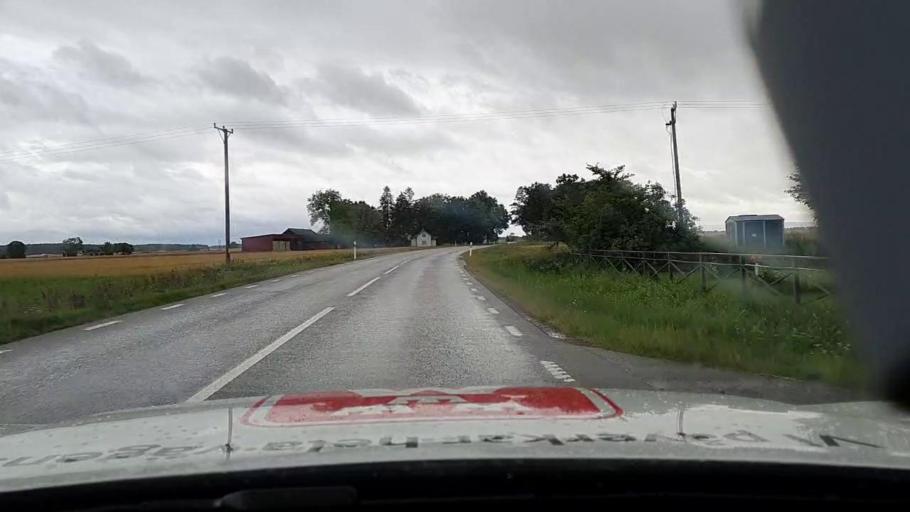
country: SE
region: Vaestra Goetaland
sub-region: Toreboda Kommun
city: Toereboda
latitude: 58.6199
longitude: 14.0135
